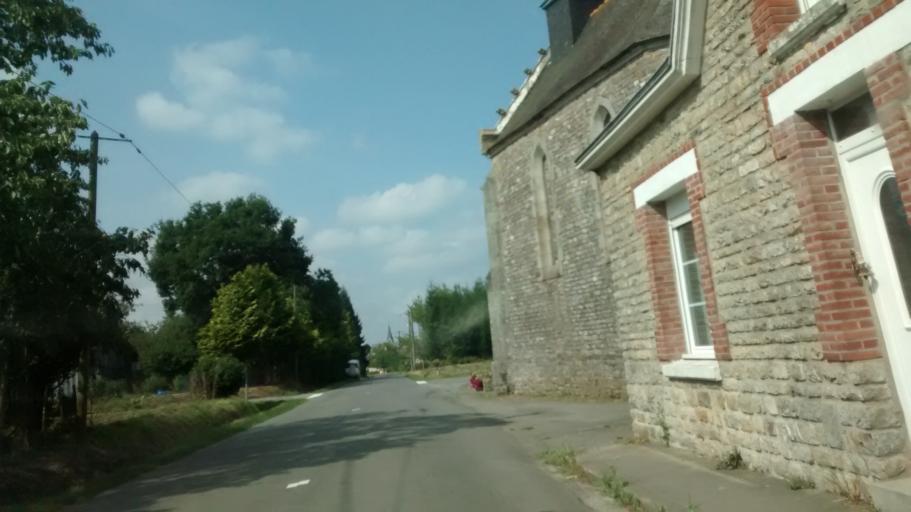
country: FR
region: Brittany
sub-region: Departement d'Ille-et-Vilaine
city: Livre-sur-Changeon
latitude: 48.2346
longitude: -1.2943
